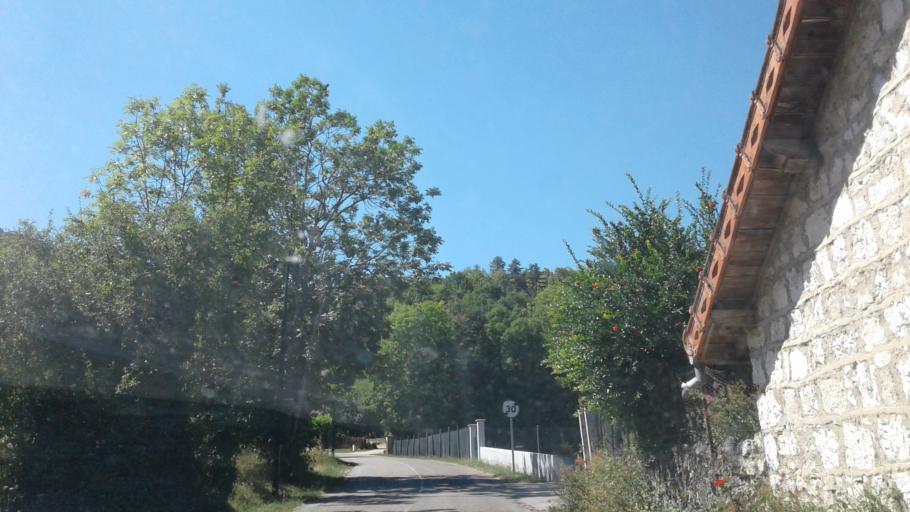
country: FR
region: Rhone-Alpes
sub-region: Departement de l'Ain
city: Artemare
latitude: 45.8761
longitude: 5.6697
